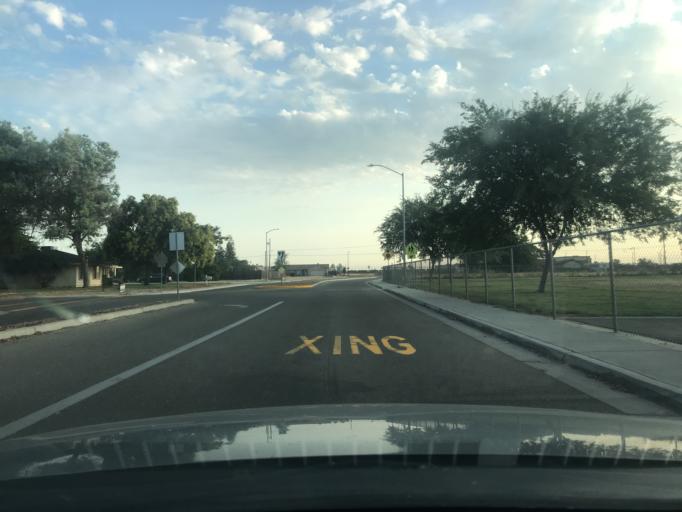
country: US
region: California
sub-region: Merced County
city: Merced
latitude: 37.3301
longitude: -120.5364
